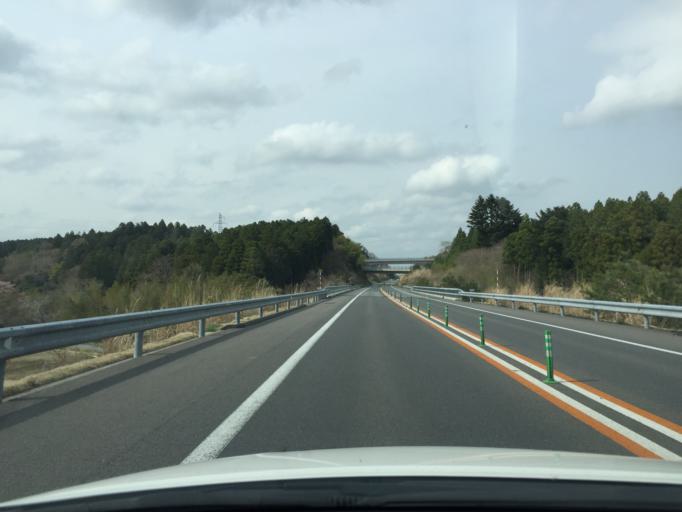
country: JP
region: Fukushima
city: Namie
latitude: 37.3238
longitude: 140.9907
